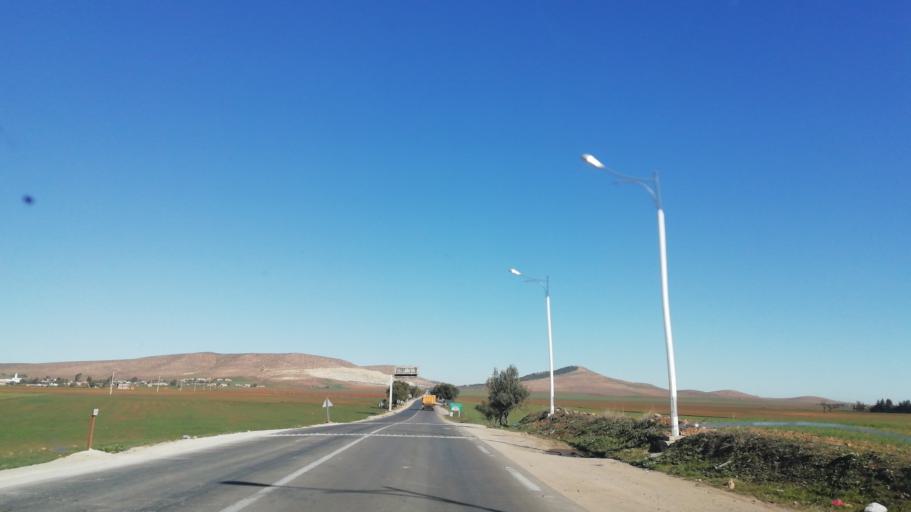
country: DZ
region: Mascara
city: Mascara
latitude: 35.2169
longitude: 0.1123
